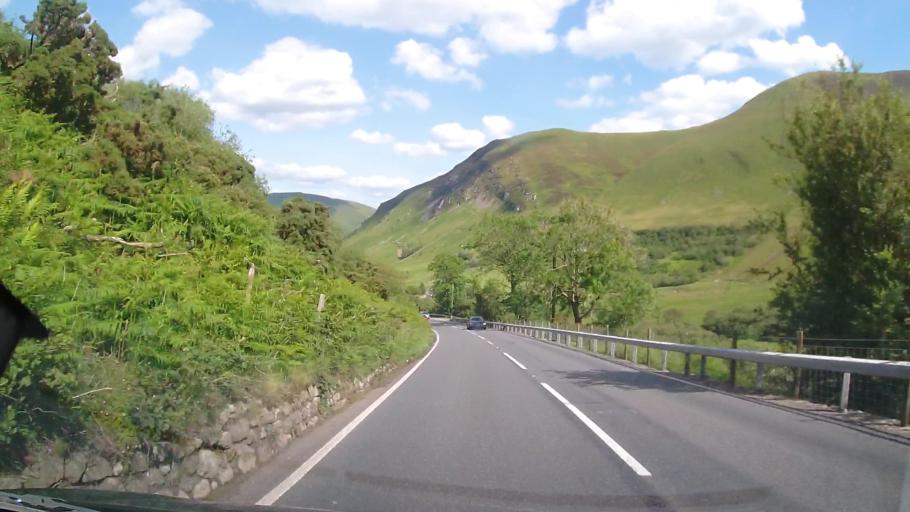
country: GB
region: Wales
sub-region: Gwynedd
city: Corris
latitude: 52.7315
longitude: -3.7573
